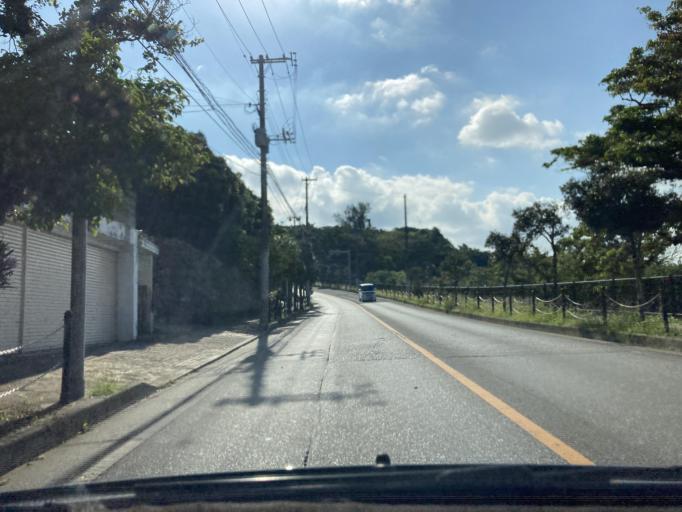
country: JP
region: Okinawa
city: Naha-shi
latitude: 26.2101
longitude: 127.7199
